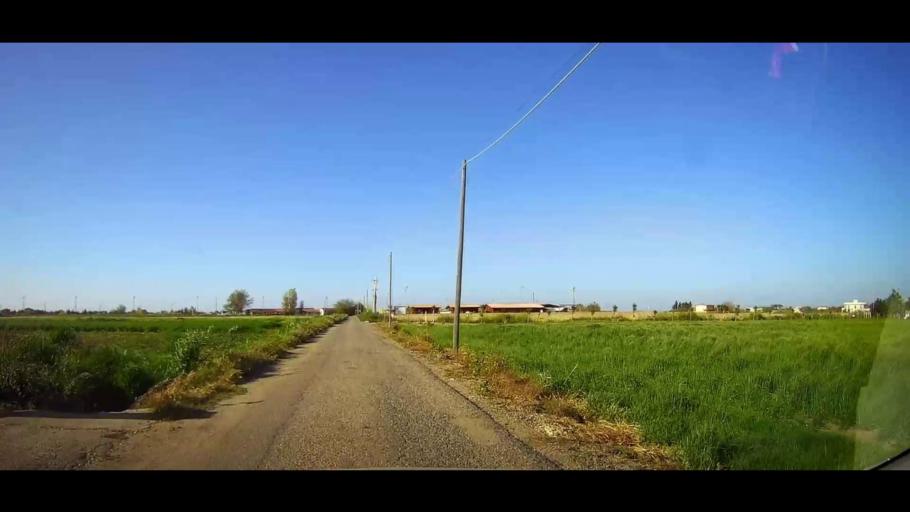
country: IT
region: Calabria
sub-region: Provincia di Crotone
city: Crotone
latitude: 39.0232
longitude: 17.1871
